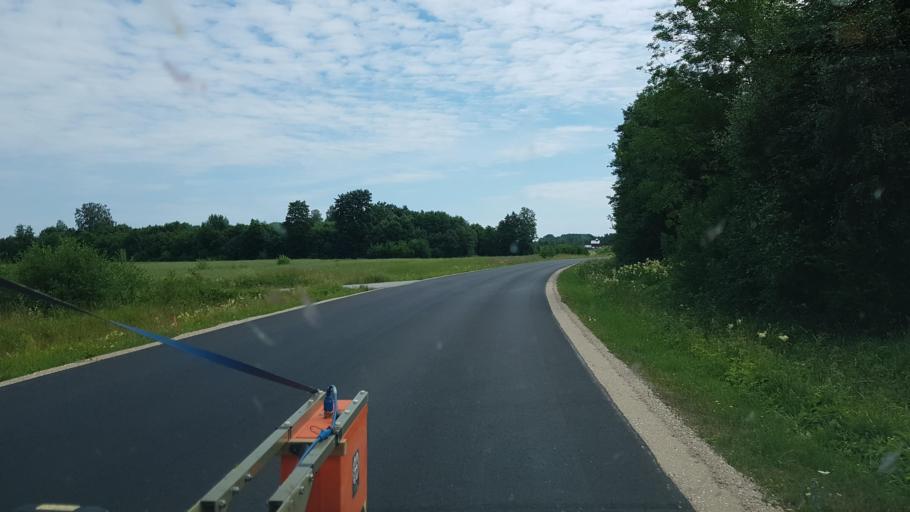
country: EE
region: Paernumaa
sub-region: Halinga vald
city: Parnu-Jaagupi
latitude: 58.6205
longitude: 24.3188
